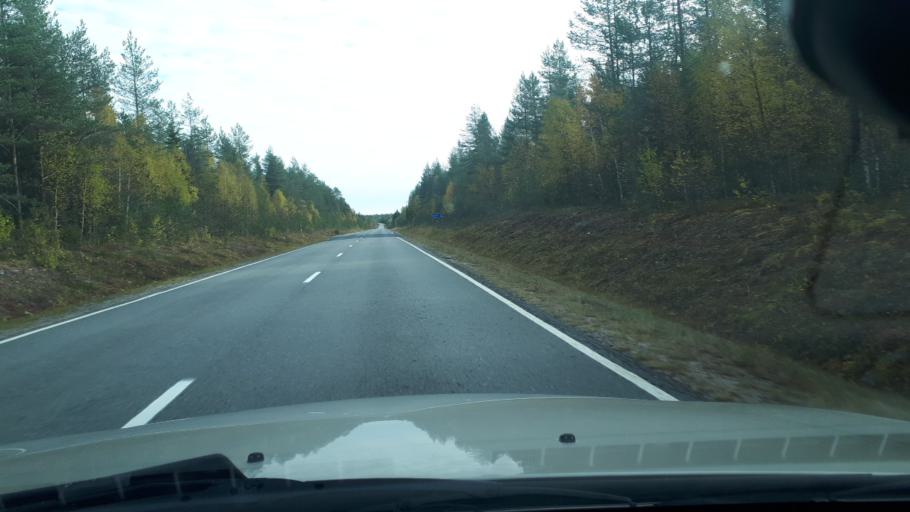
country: FI
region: Northern Ostrobothnia
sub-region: Oulu
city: Yli-Ii
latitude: 65.9250
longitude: 25.8190
